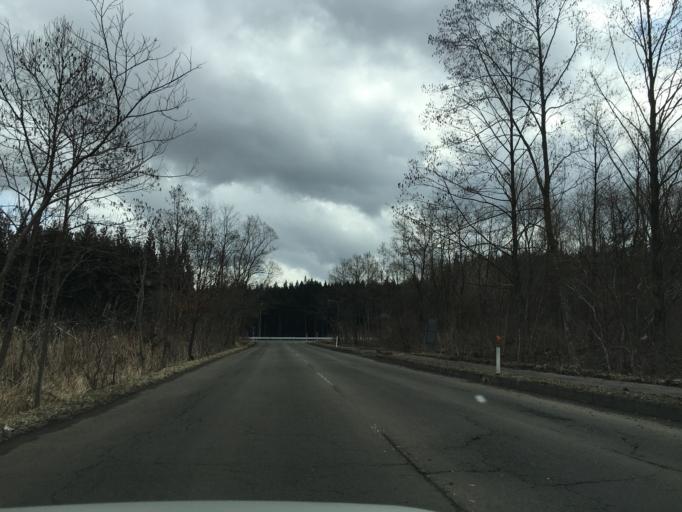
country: JP
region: Akita
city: Takanosu
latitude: 40.1807
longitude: 140.3513
